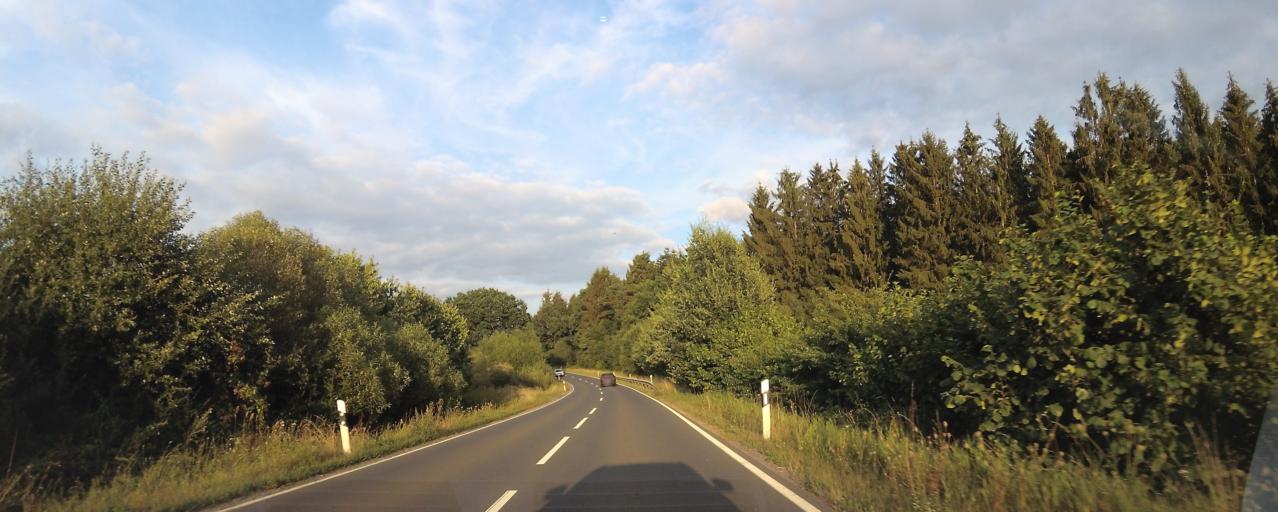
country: DE
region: Rheinland-Pfalz
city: Beilingen
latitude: 49.9445
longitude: 6.6729
